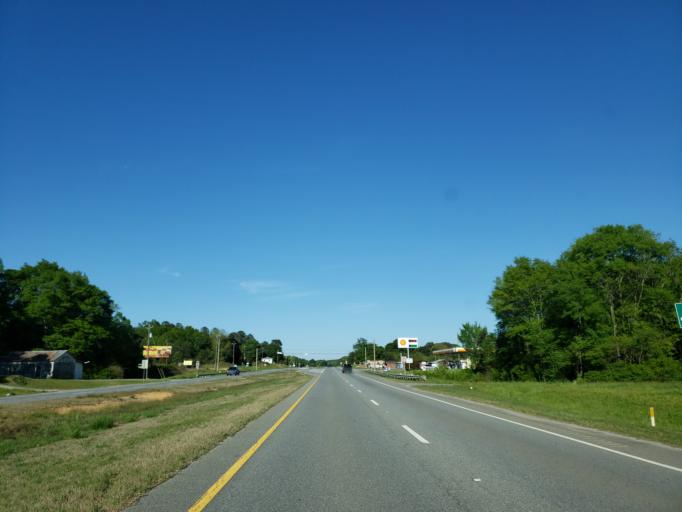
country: US
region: Georgia
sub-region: Polk County
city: Aragon
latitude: 34.0065
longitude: -85.1432
